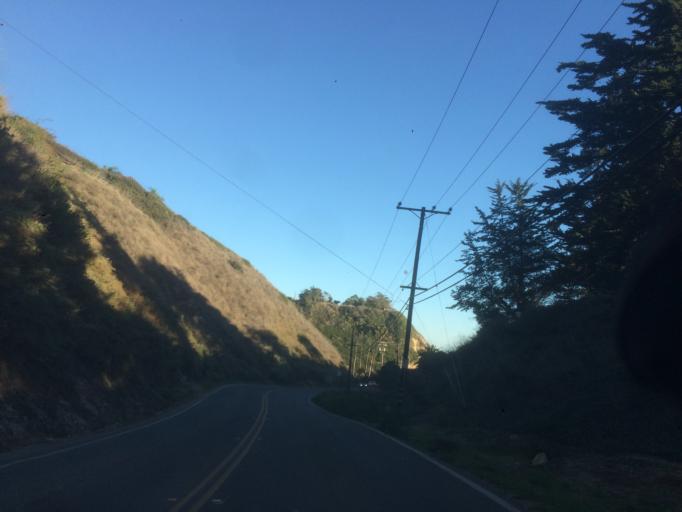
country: US
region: California
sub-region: Santa Barbara County
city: Santa Barbara
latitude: 34.4048
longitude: -119.7459
